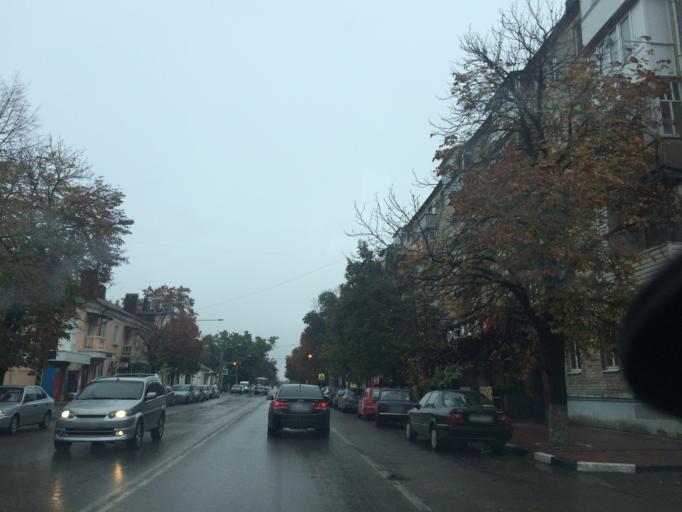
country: RU
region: Rostov
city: Azov
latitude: 47.1112
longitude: 39.4245
